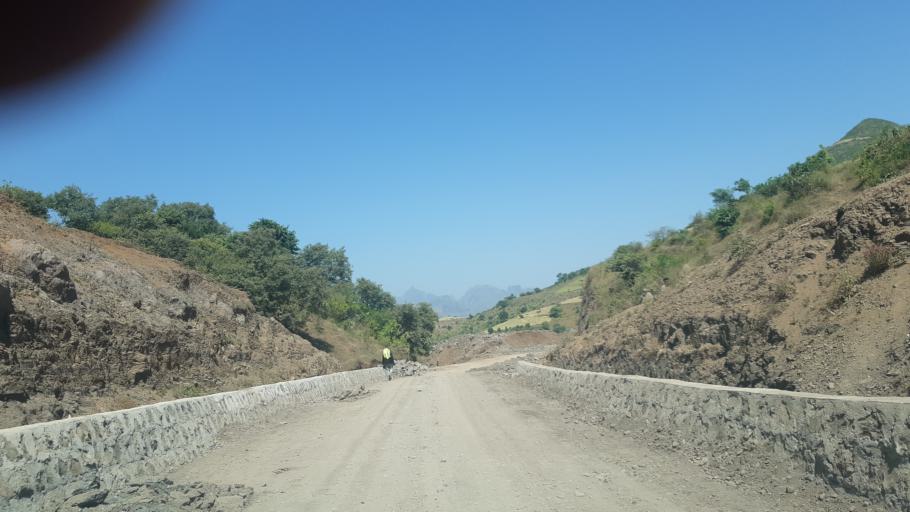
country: ET
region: Amhara
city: Dabat
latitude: 13.1641
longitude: 37.6059
